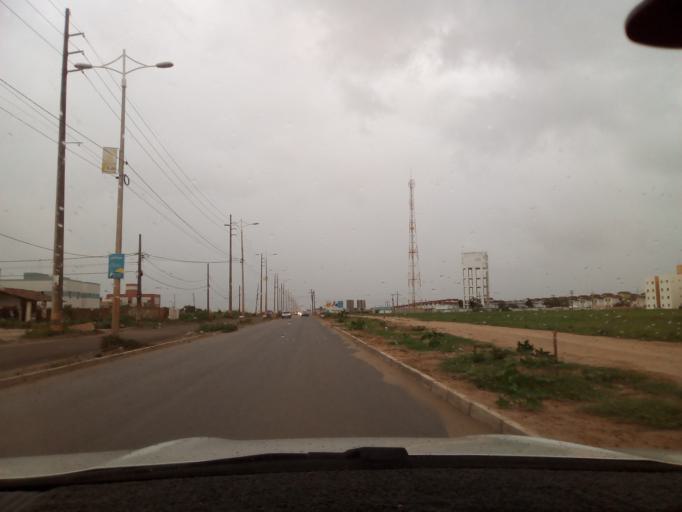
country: BR
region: Paraiba
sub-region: Conde
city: Conde
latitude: -7.1997
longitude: -34.8748
